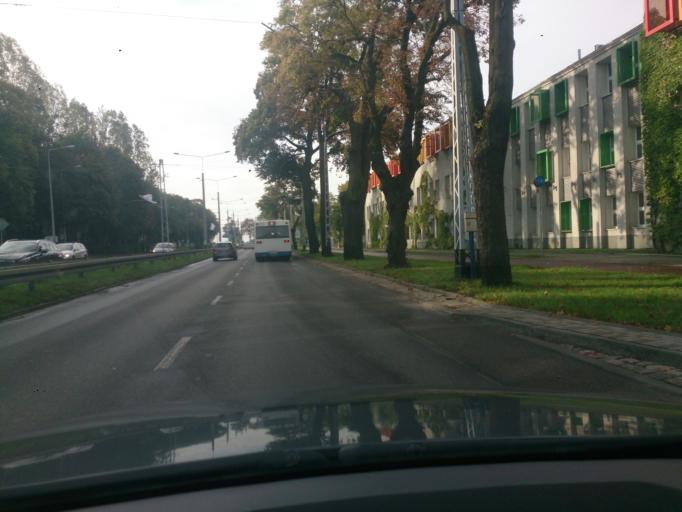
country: PL
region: Pomeranian Voivodeship
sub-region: Gdynia
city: Gdynia
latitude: 54.4966
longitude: 18.5384
